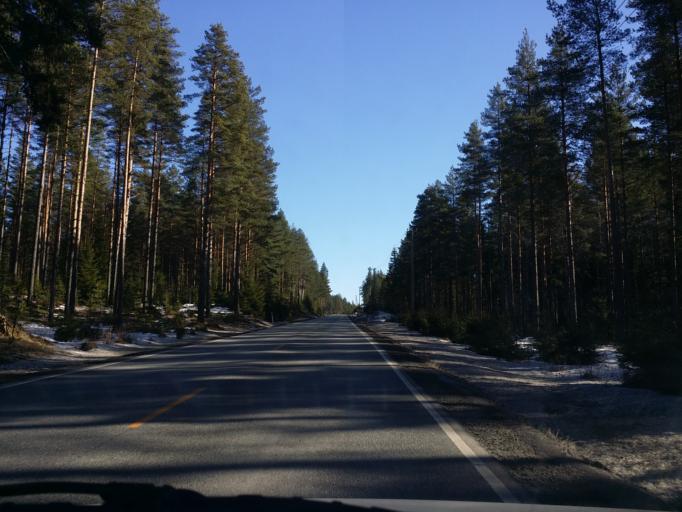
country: NO
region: Buskerud
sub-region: Ringerike
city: Honefoss
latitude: 60.3188
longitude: 10.1411
